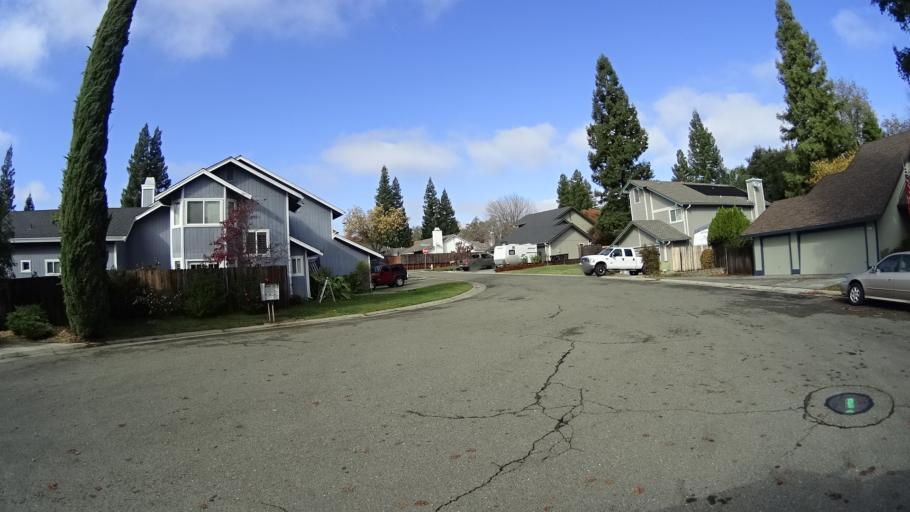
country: US
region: California
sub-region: Sacramento County
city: Antelope
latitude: 38.6872
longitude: -121.3247
